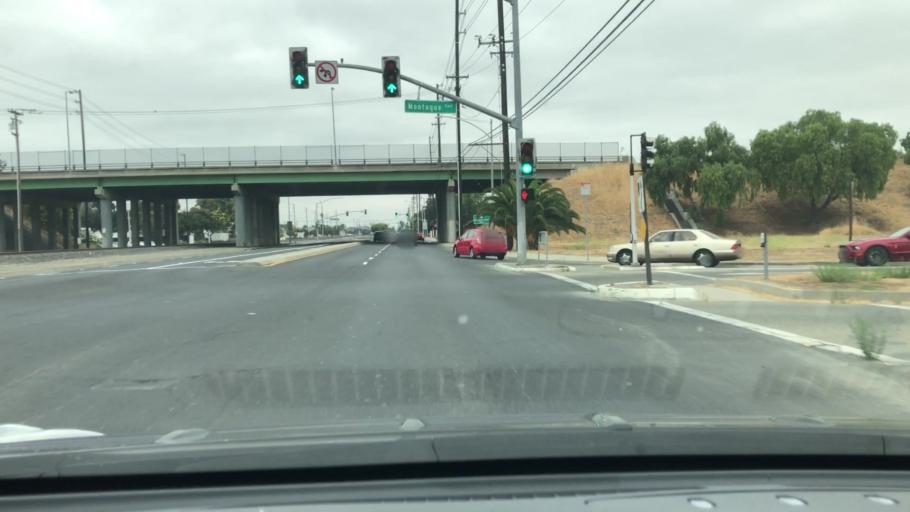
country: US
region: California
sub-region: Santa Clara County
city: Santa Clara
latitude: 37.3885
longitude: -121.9543
